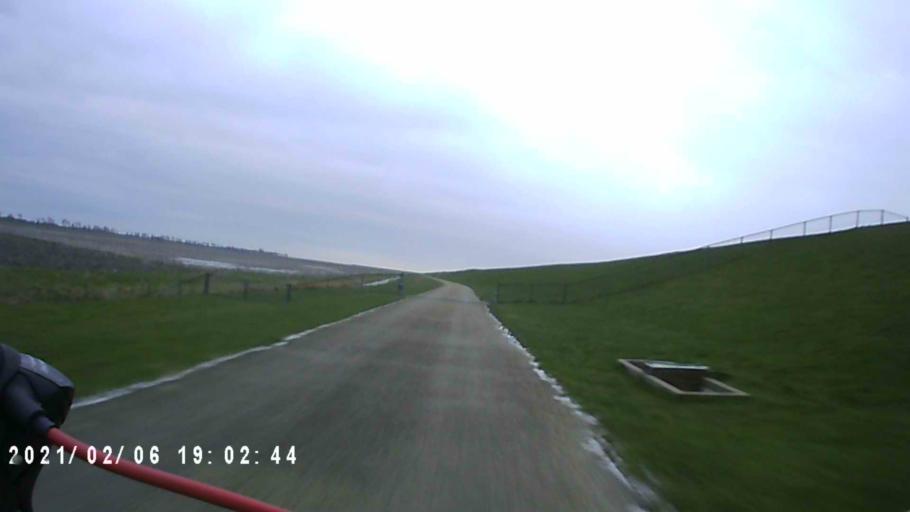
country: NL
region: Groningen
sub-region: Gemeente Winsum
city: Winsum
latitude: 53.4234
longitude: 6.4818
